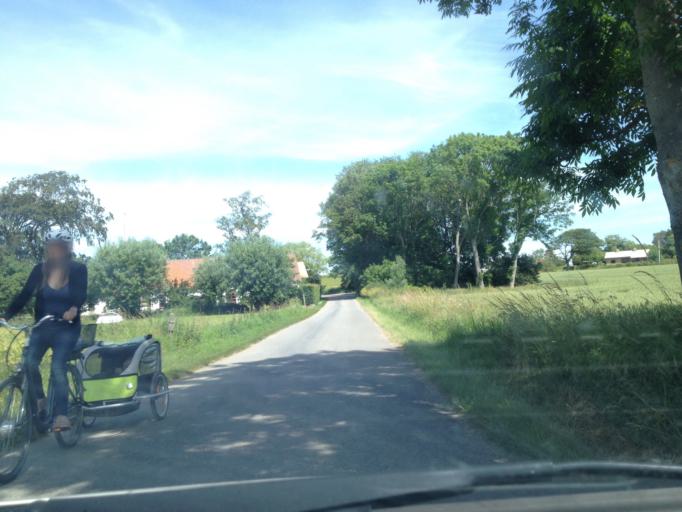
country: DK
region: Central Jutland
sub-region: Samso Kommune
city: Tranebjerg
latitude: 55.8761
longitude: 10.6735
